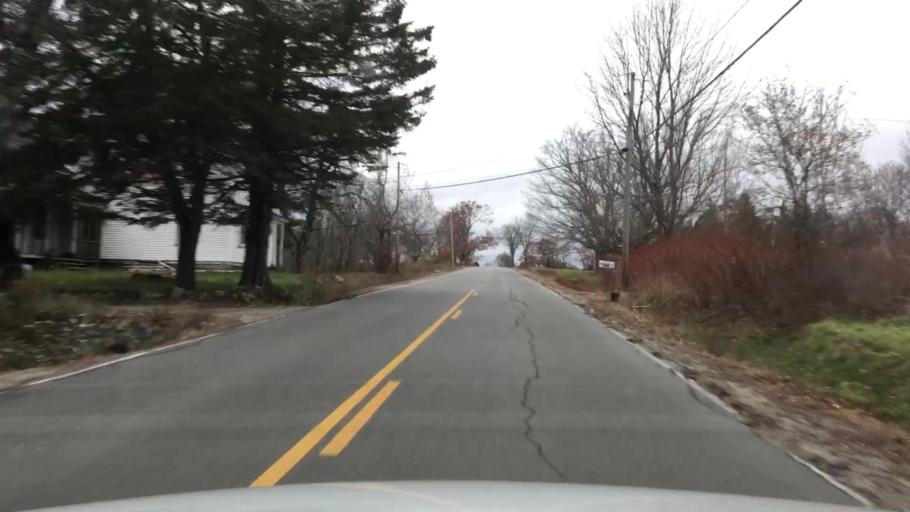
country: US
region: Maine
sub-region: Hancock County
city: Penobscot
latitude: 44.4362
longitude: -68.6323
